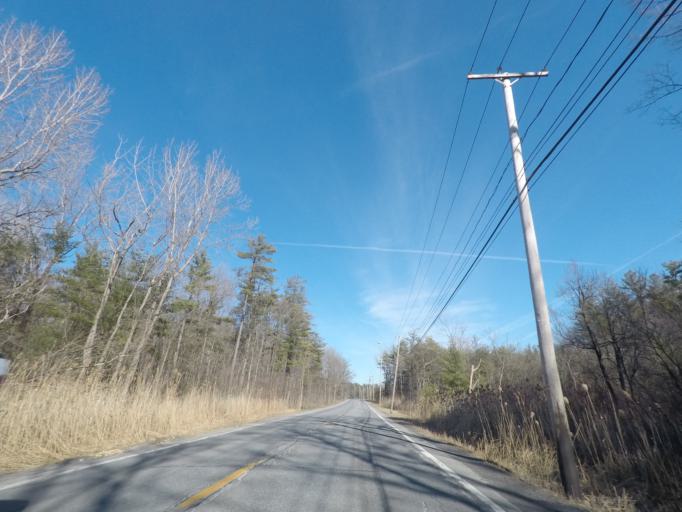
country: US
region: New York
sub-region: Saratoga County
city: Milton
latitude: 43.0755
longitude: -73.8421
